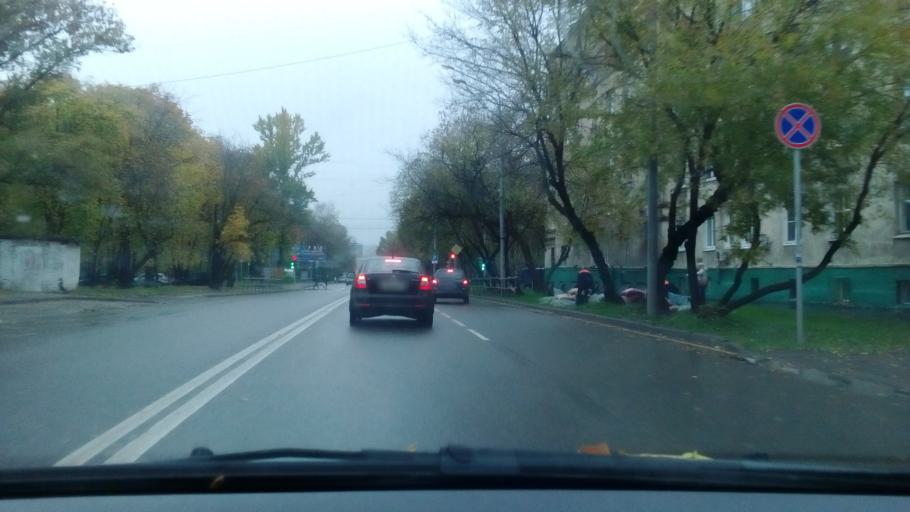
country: RU
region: Moscow
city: Mar'ina Roshcha
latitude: 55.7987
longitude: 37.5759
